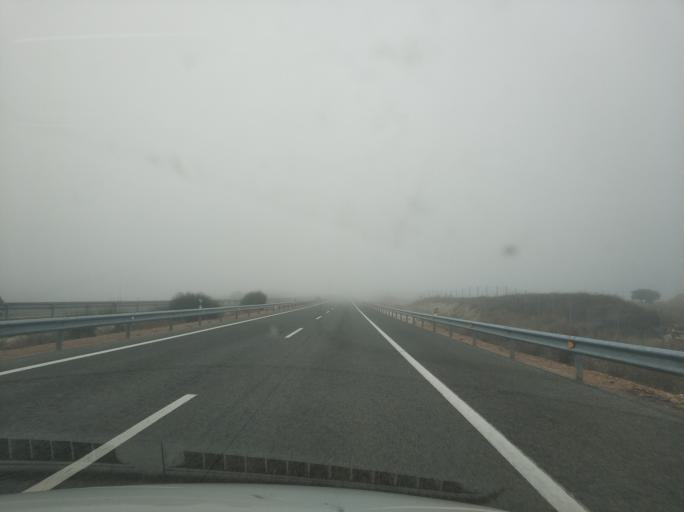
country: ES
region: Castille and Leon
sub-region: Provincia de Soria
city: Adradas
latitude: 41.3326
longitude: -2.4816
